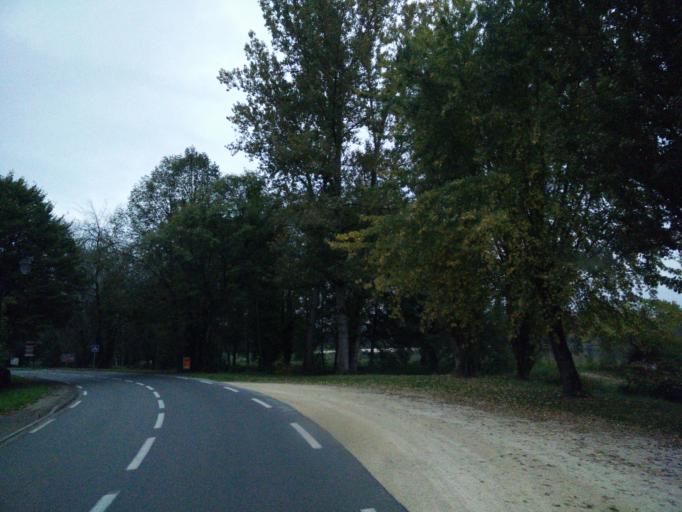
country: FR
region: Aquitaine
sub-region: Departement de la Dordogne
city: Carsac-Aillac
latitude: 44.8063
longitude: 1.2971
